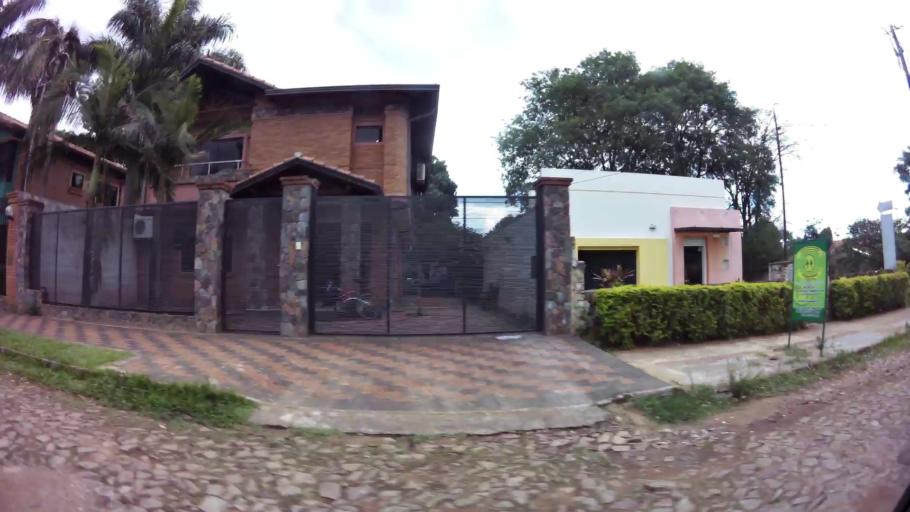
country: PY
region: Central
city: San Lorenzo
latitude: -25.2726
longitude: -57.5034
